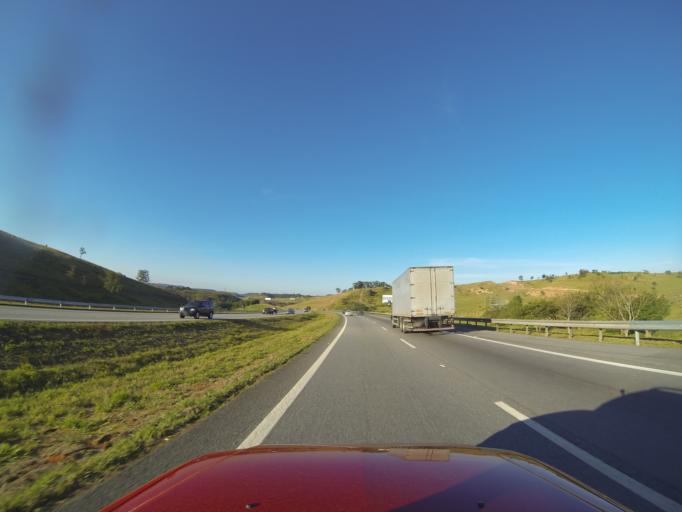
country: BR
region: Sao Paulo
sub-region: Jacarei
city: Jacarei
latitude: -23.3154
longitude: -45.9021
